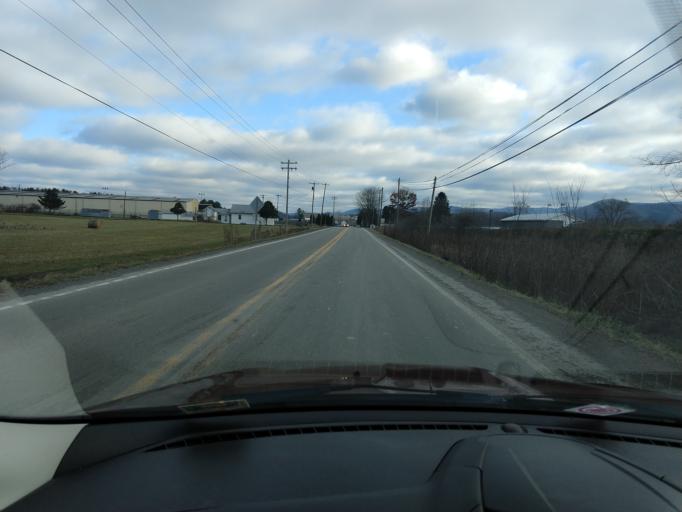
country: US
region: West Virginia
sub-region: Randolph County
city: Elkins
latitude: 38.7992
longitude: -79.8956
